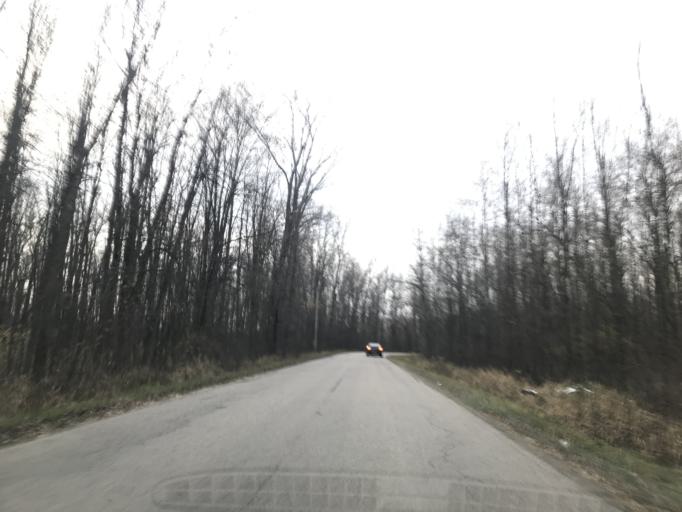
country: US
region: Wisconsin
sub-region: Marinette County
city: Peshtigo
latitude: 45.0636
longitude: -87.7994
